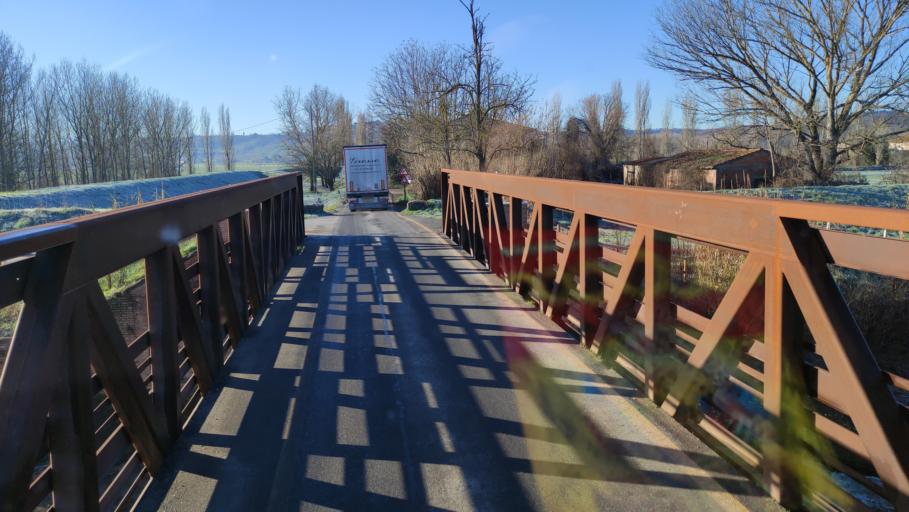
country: IT
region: Tuscany
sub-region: Province of Florence
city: Castelfiorentino
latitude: 43.6478
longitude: 10.9472
